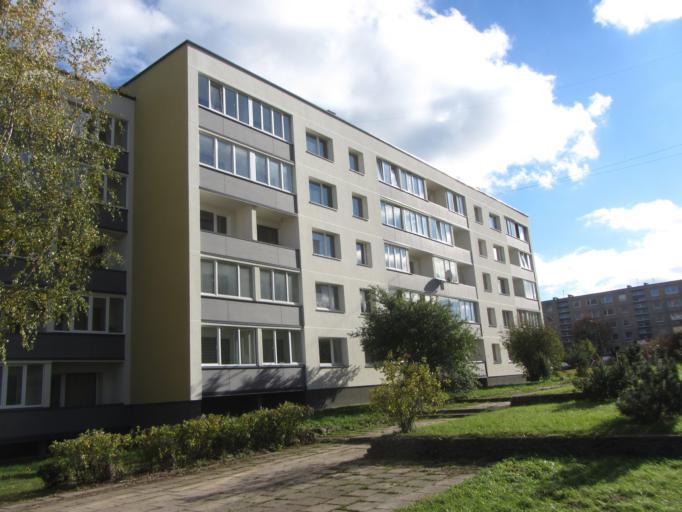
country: LT
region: Vilnius County
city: Lazdynai
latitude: 54.6747
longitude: 25.2078
